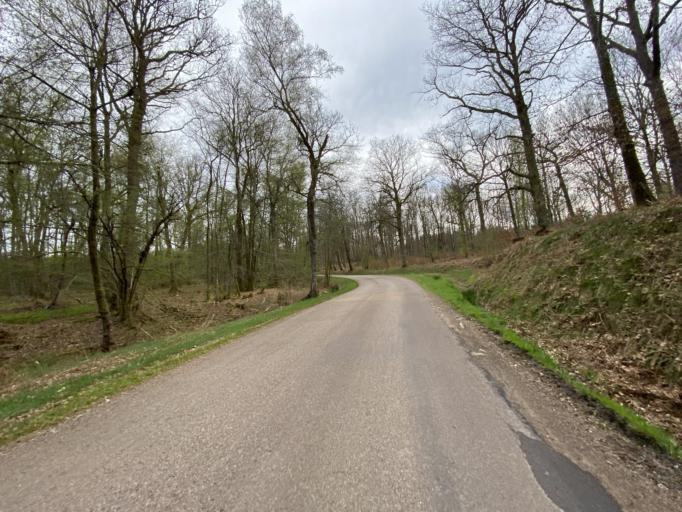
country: FR
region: Bourgogne
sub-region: Departement de la Cote-d'Or
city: Saulieu
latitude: 47.3054
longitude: 4.0880
